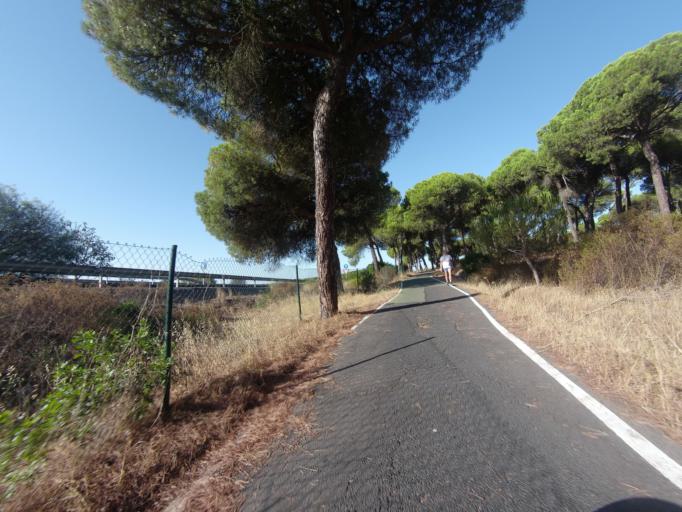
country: ES
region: Andalusia
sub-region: Provincia de Huelva
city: Aljaraque
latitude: 37.2179
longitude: -7.0243
